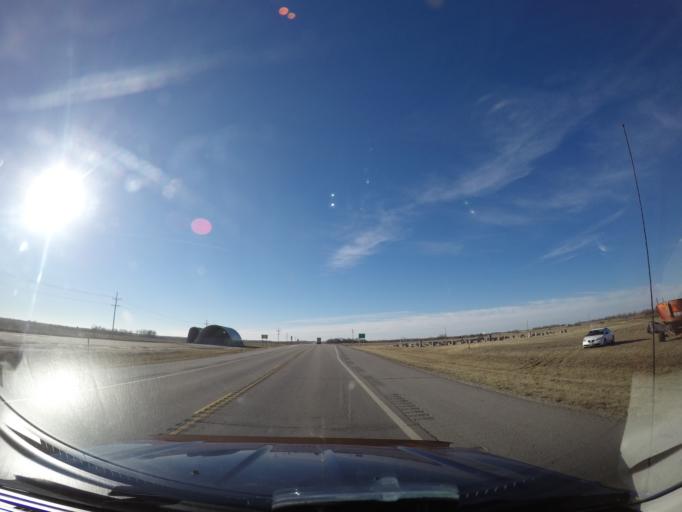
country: US
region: Kansas
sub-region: Marion County
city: Hillsboro
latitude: 38.3624
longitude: -97.3054
